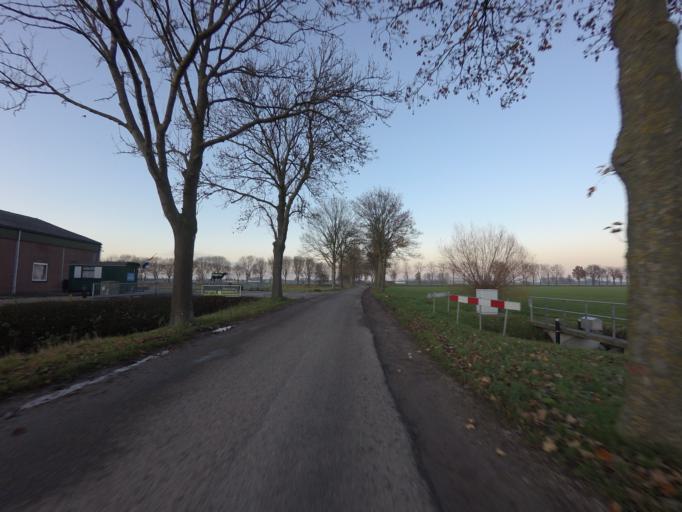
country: NL
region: Gelderland
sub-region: Gemeente Maasdriel
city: Hedel
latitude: 51.7621
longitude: 5.2252
